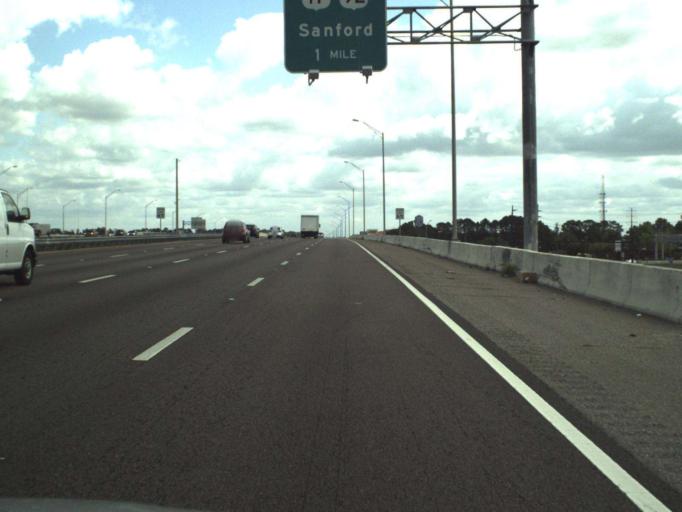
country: US
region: Florida
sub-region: Seminole County
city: Lake Mary
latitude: 28.8092
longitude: -81.3386
